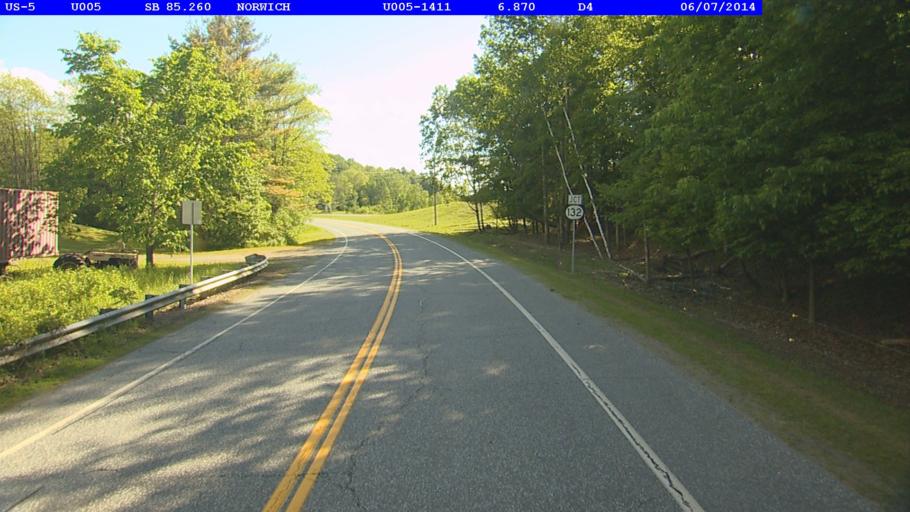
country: US
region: New Hampshire
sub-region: Grafton County
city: Hanover
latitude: 43.7588
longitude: -72.2280
